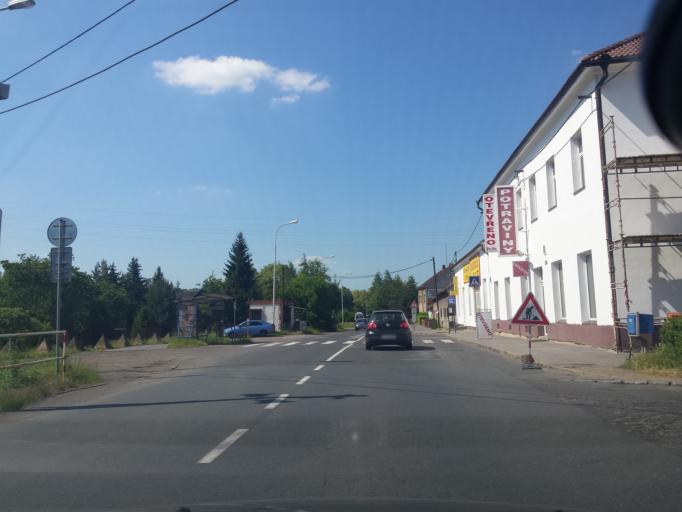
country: CZ
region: Central Bohemia
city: Kralupy nad Vltavou
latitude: 50.2275
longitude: 14.2970
